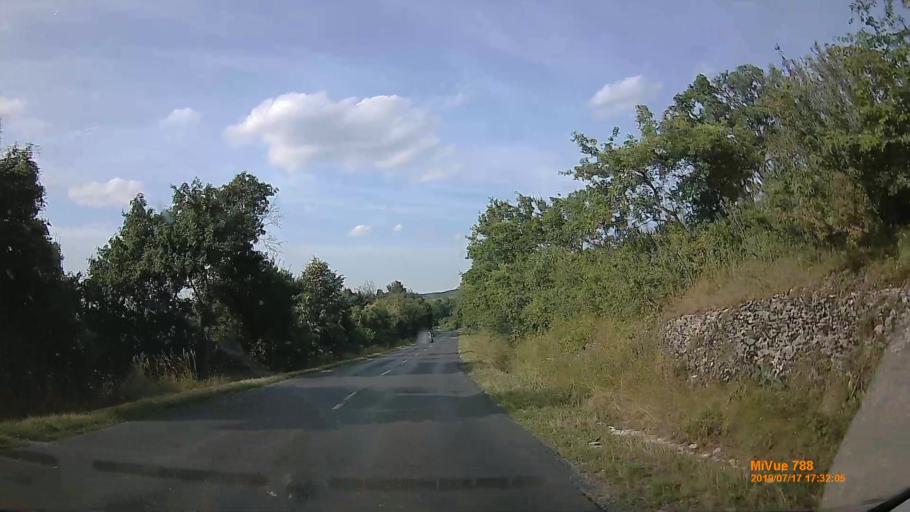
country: HU
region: Veszprem
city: Ajka
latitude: 47.0372
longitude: 17.5570
